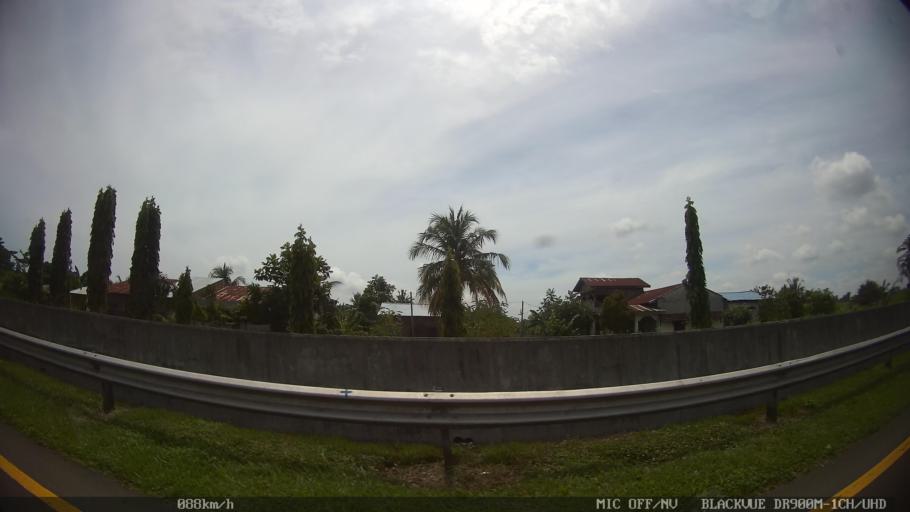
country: ID
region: North Sumatra
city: Labuhan Deli
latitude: 3.7151
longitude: 98.6824
